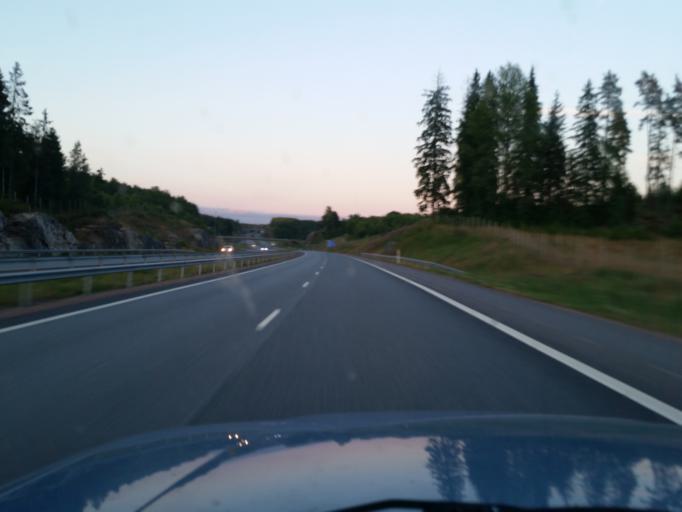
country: FI
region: Uusimaa
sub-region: Helsinki
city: Sammatti
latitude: 60.3796
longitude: 23.7904
